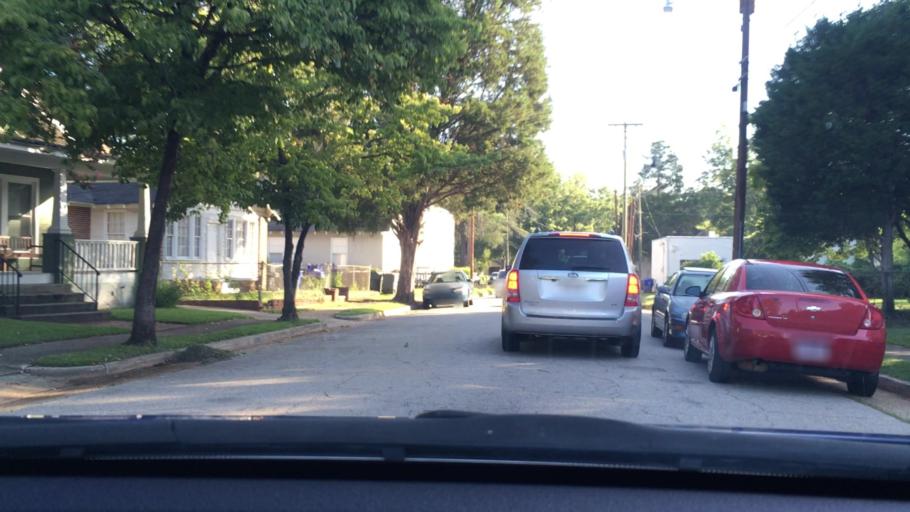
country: US
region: South Carolina
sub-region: Richland County
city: Columbia
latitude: 34.0217
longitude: -81.0463
